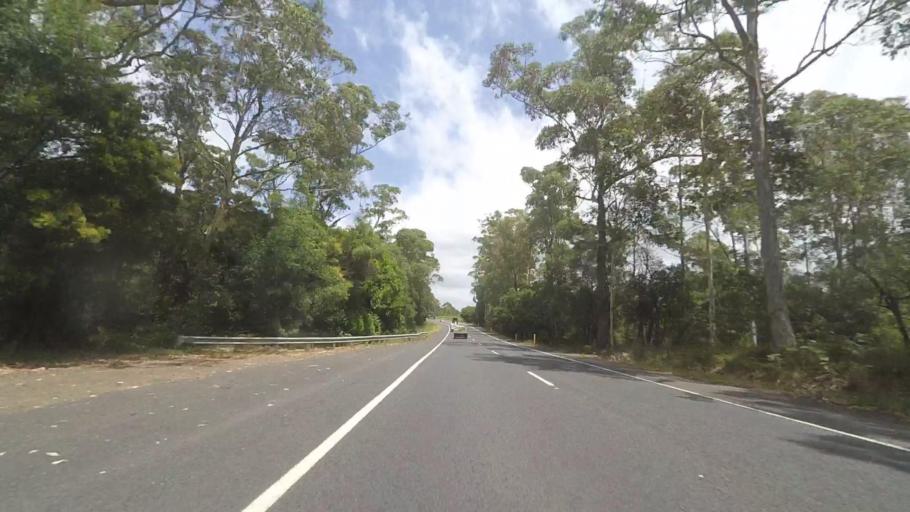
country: AU
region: New South Wales
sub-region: Shoalhaven Shire
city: Falls Creek
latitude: -35.0811
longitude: 150.5467
